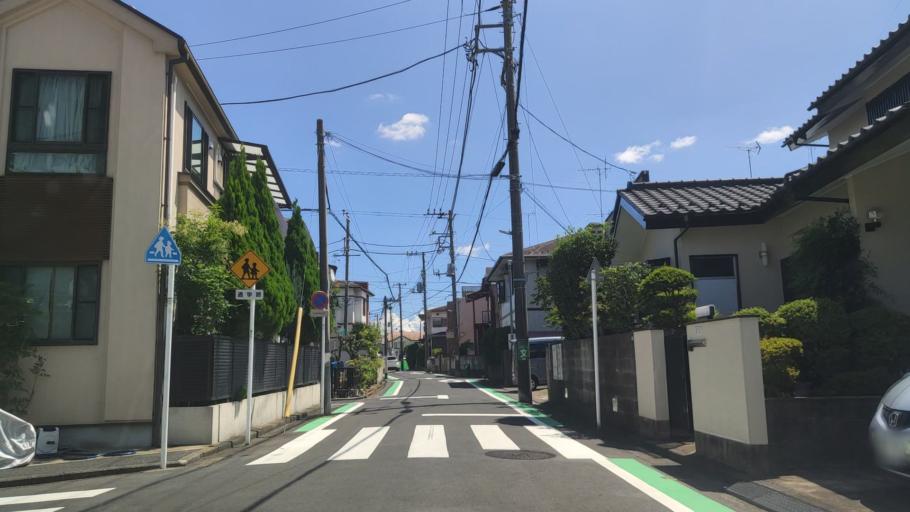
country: JP
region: Kanagawa
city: Yokohama
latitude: 35.5296
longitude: 139.6290
